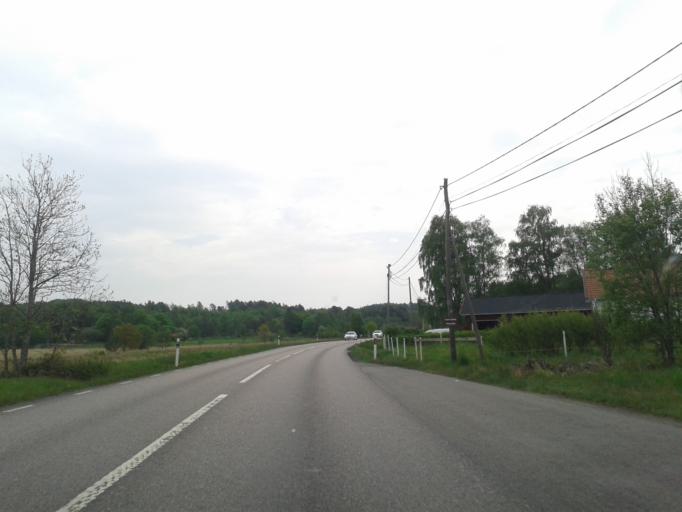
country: SE
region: Vaestra Goetaland
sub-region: Kungalvs Kommun
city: Kode
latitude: 57.8929
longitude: 11.8746
